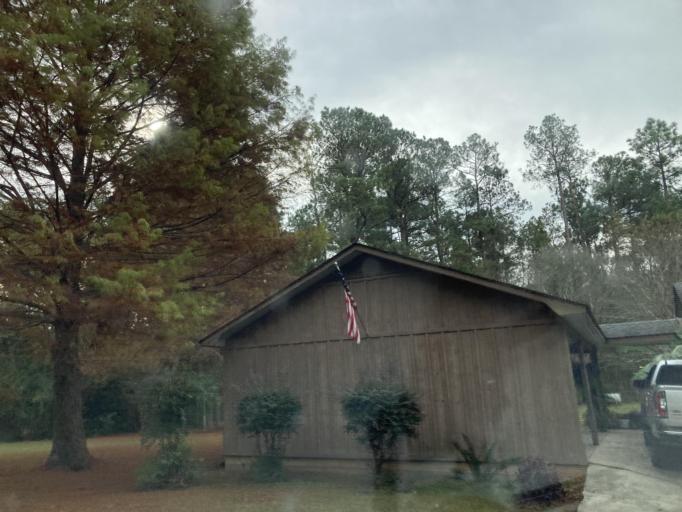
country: US
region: Mississippi
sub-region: Lamar County
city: Purvis
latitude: 31.1574
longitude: -89.4590
